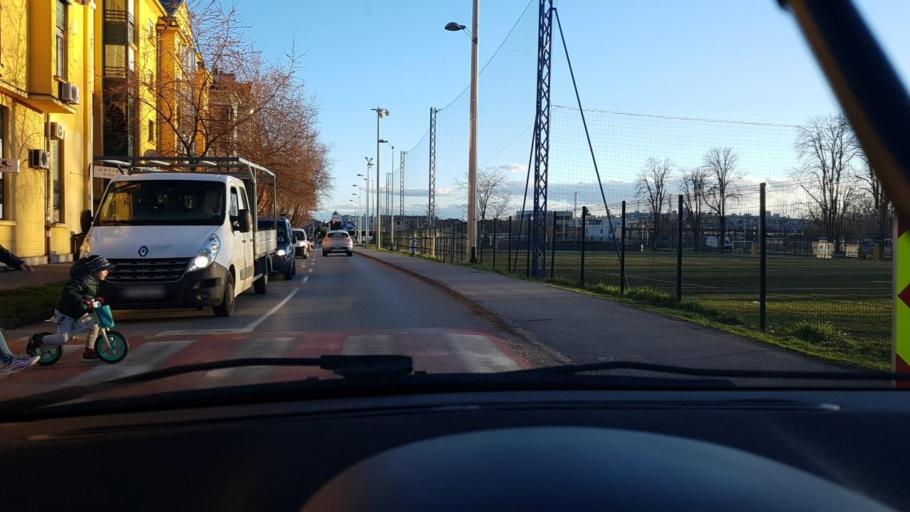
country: HR
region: Grad Zagreb
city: Stenjevec
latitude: 45.8140
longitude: 15.8984
